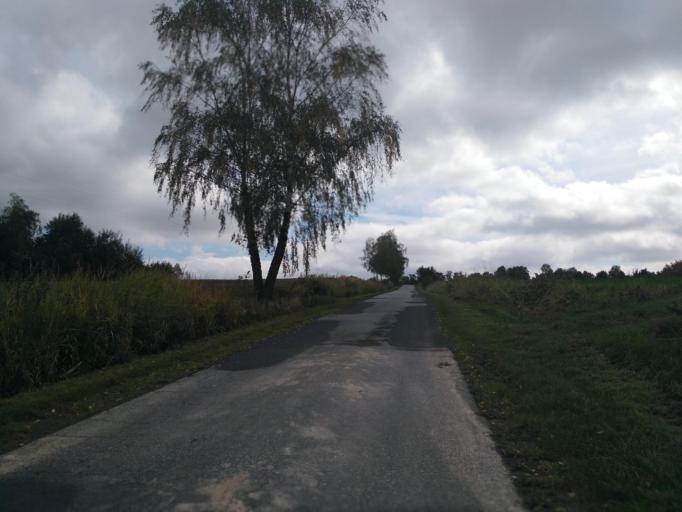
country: PL
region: Subcarpathian Voivodeship
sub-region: Powiat ropczycko-sedziszowski
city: Niedzwiada
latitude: 49.9268
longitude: 21.4825
